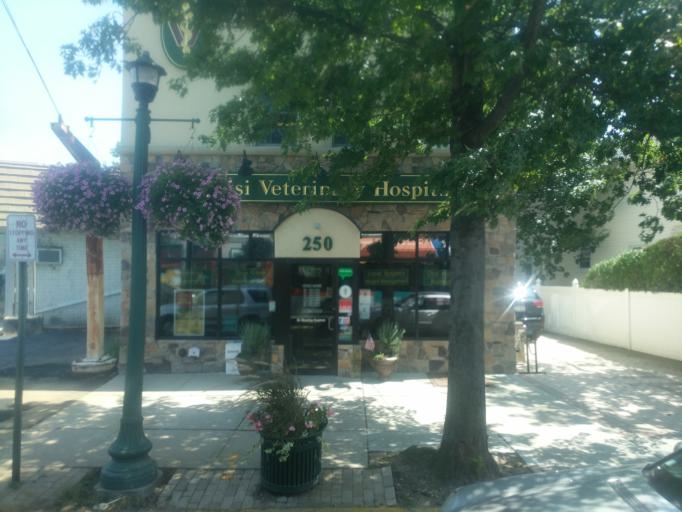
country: US
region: New York
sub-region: Nassau County
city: Malverne
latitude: 40.6744
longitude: -73.6701
